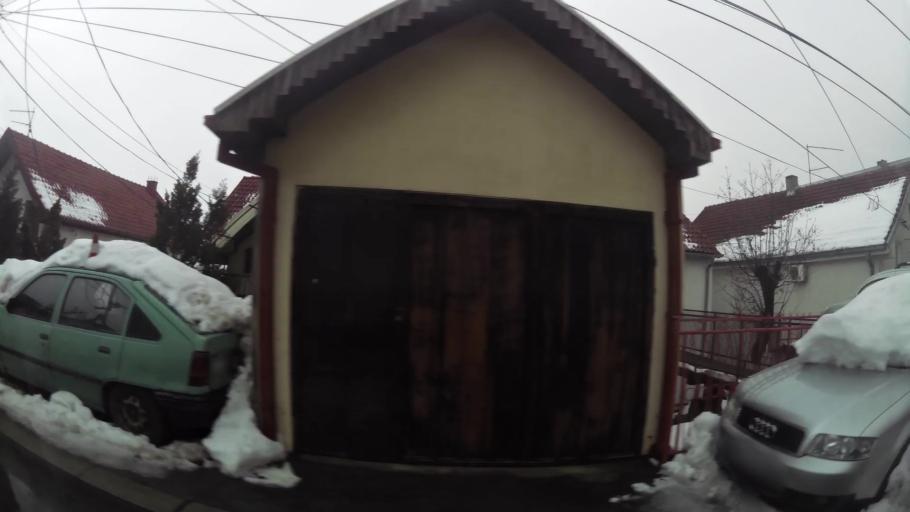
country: RS
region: Central Serbia
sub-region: Belgrade
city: Zvezdara
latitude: 44.7864
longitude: 20.5244
